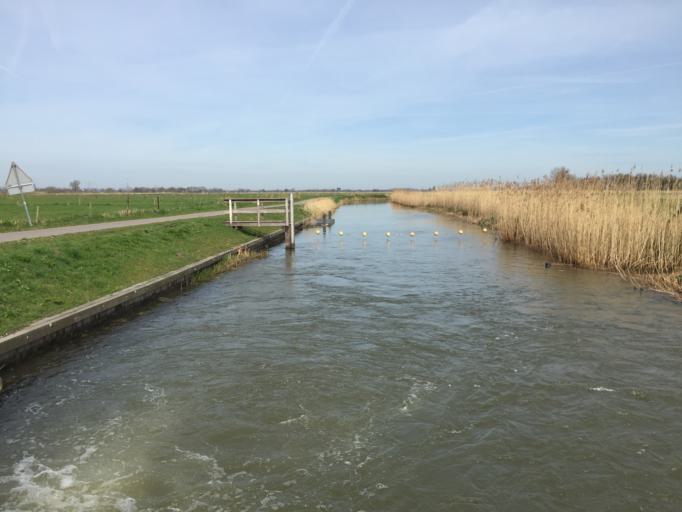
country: NL
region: Gelderland
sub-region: Gemeente Wageningen
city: Wageningen
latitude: 51.9815
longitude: 5.6160
